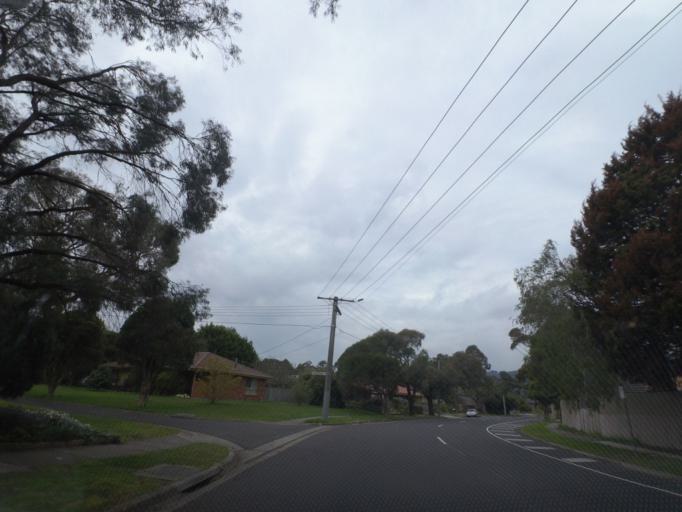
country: AU
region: Victoria
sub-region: Maroondah
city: Bayswater North
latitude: -37.8311
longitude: 145.2963
